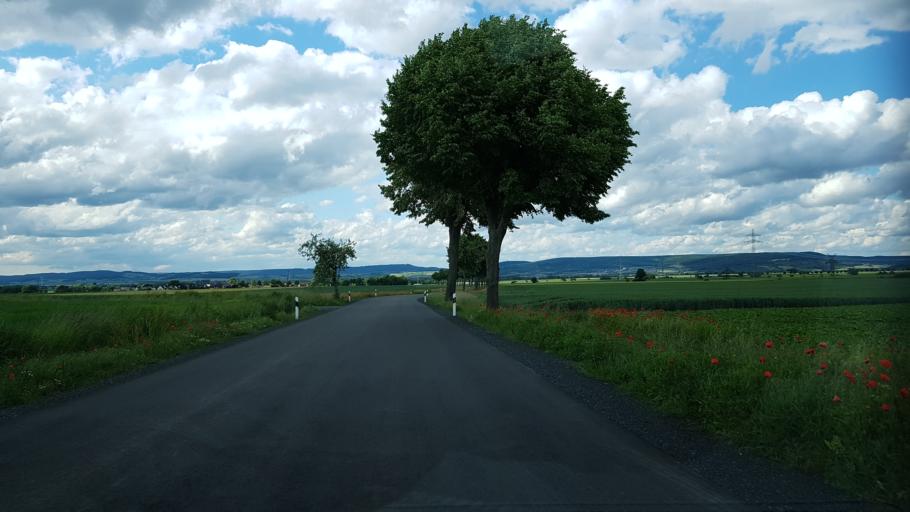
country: DE
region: Lower Saxony
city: Moringen
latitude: 51.7538
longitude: 9.8731
